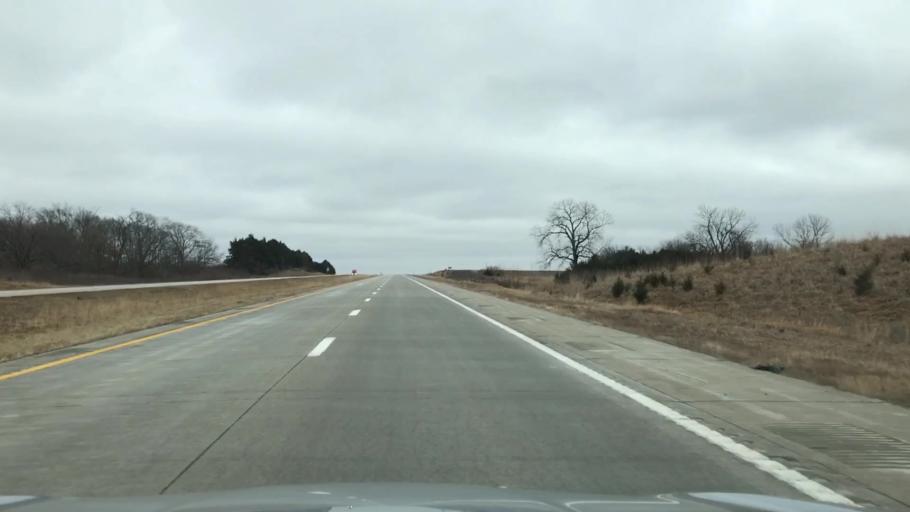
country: US
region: Missouri
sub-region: Caldwell County
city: Hamilton
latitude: 39.7351
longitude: -93.8601
